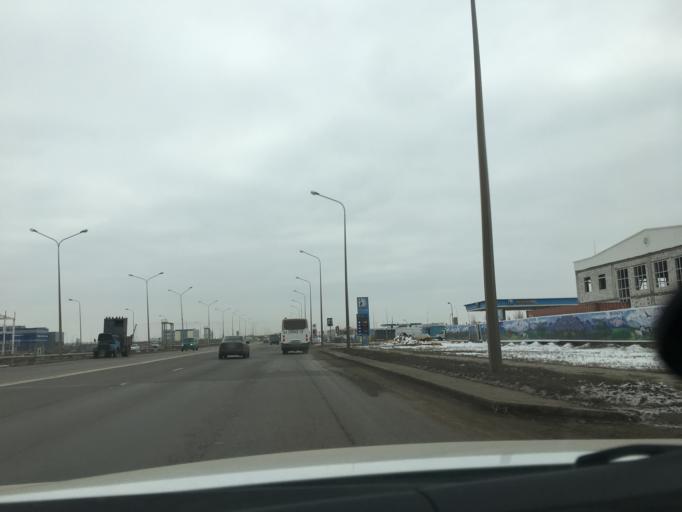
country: KZ
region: Astana Qalasy
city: Astana
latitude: 51.1583
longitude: 71.5240
